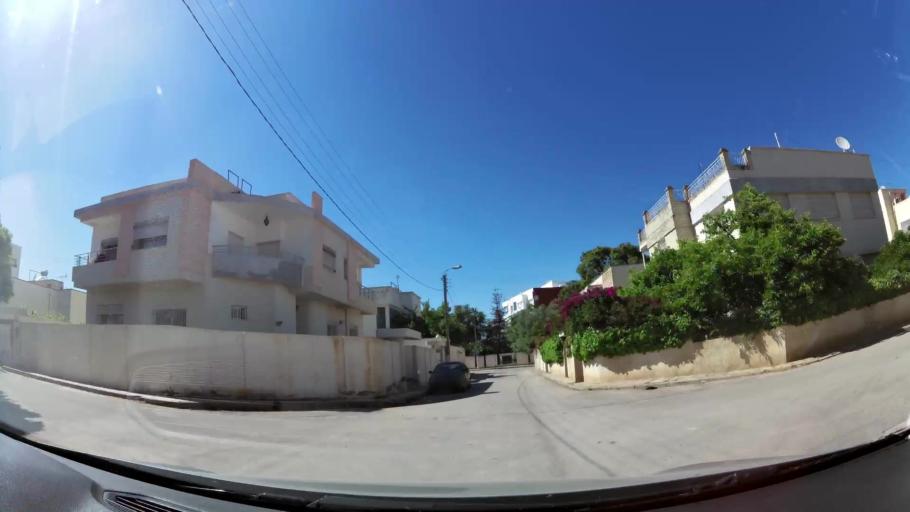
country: MA
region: Fes-Boulemane
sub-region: Fes
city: Fes
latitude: 34.0221
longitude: -4.9910
